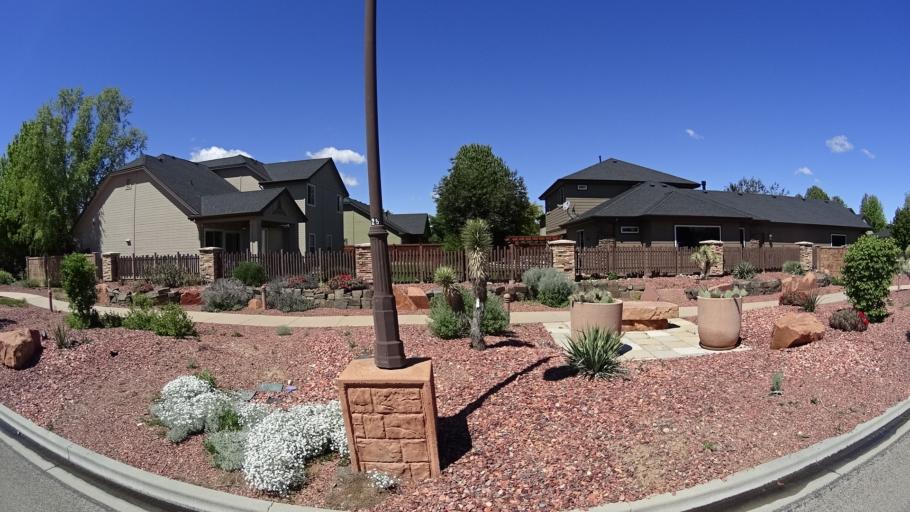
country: US
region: Idaho
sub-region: Ada County
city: Meridian
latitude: 43.6518
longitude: -116.3847
